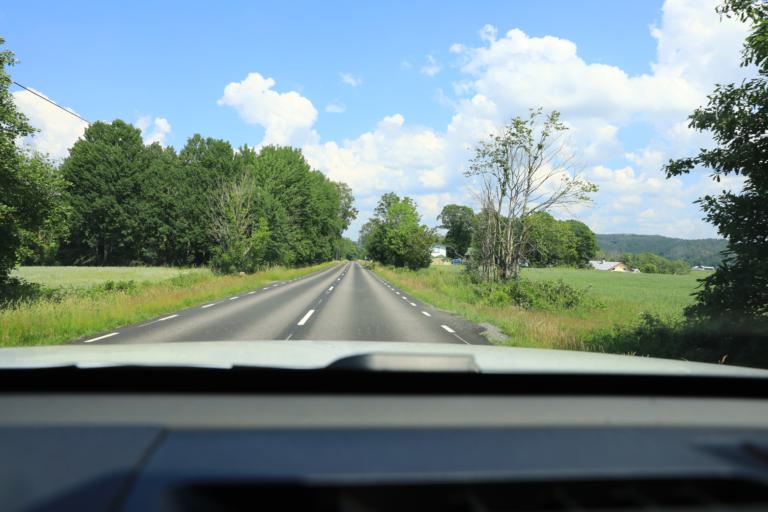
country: SE
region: Halland
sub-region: Varbergs Kommun
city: Veddige
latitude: 57.2043
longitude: 12.2964
